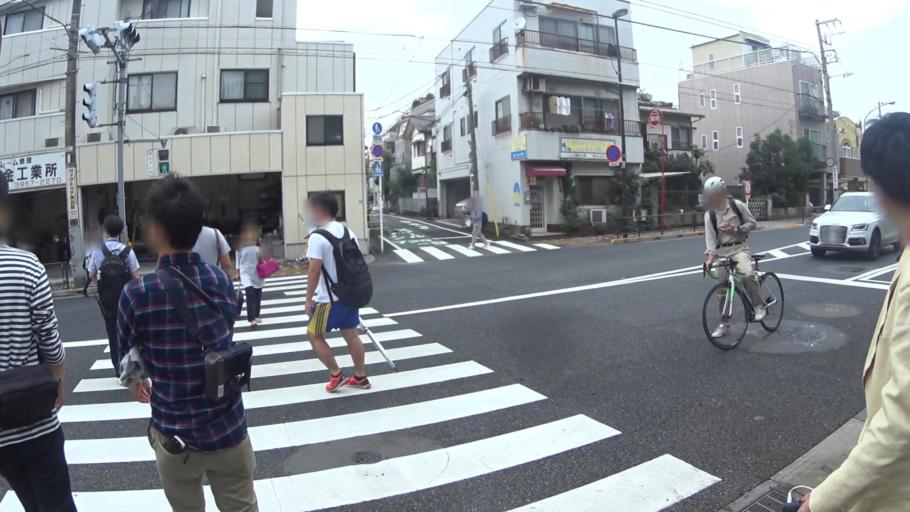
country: JP
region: Tokyo
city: Tokyo
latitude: 35.7368
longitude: 139.6824
